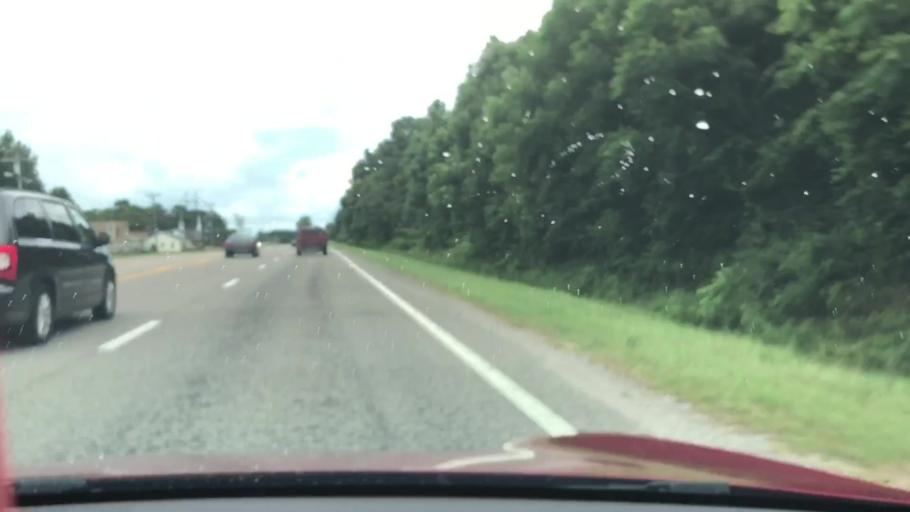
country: US
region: North Carolina
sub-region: Dare County
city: Southern Shores
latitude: 36.1836
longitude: -75.8641
